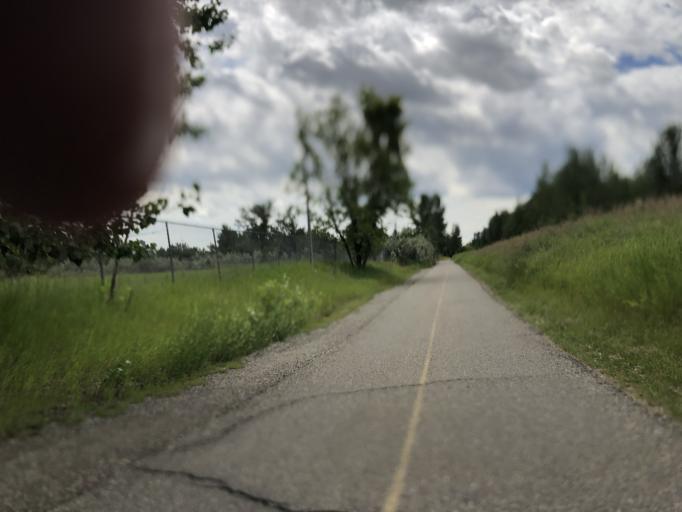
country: CA
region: Alberta
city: Calgary
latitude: 51.0265
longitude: -114.0114
